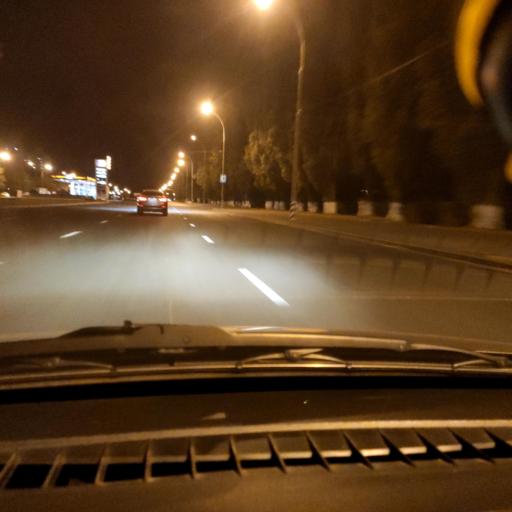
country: RU
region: Samara
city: Tol'yatti
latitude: 53.5059
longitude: 49.2757
